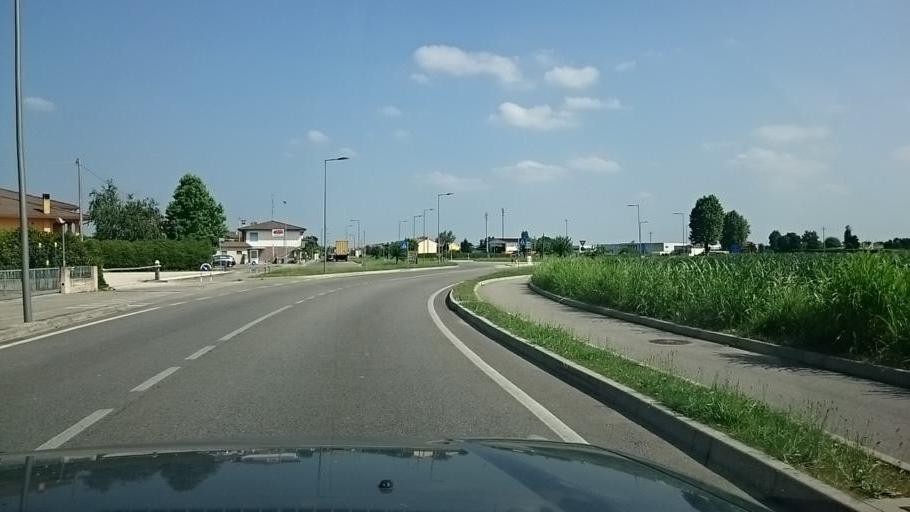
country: IT
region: Veneto
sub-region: Provincia di Padova
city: Abbazia Pisani
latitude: 45.6137
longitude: 11.8526
